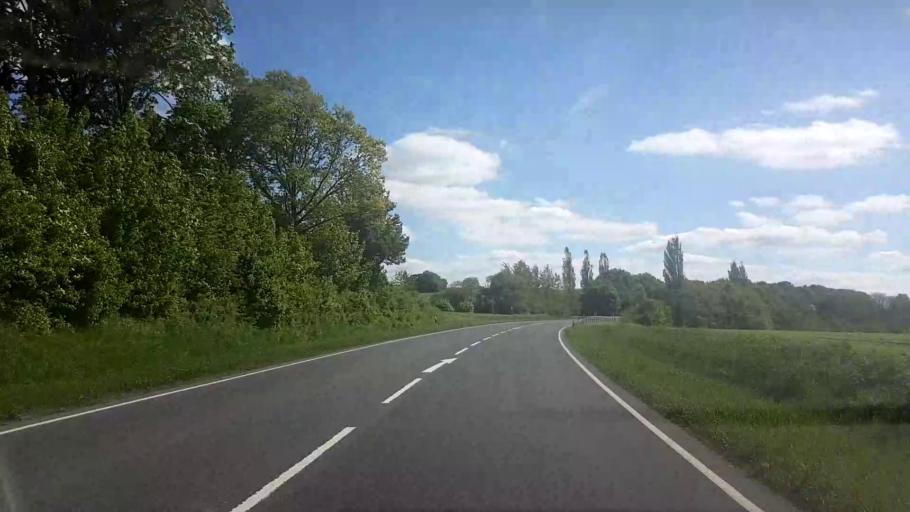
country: DE
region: Bavaria
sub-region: Regierungsbezirk Unterfranken
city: Untermerzbach
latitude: 50.0985
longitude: 10.8663
